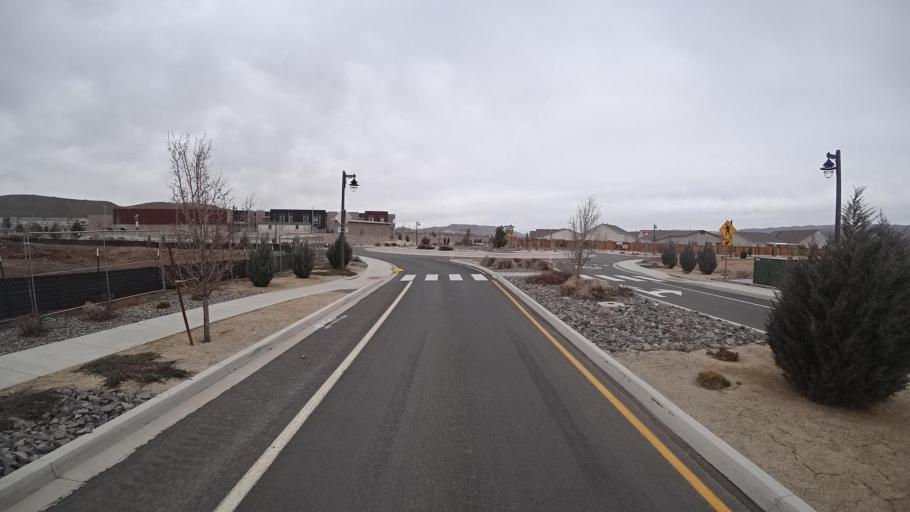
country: US
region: Nevada
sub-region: Washoe County
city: Spanish Springs
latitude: 39.6081
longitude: -119.7207
